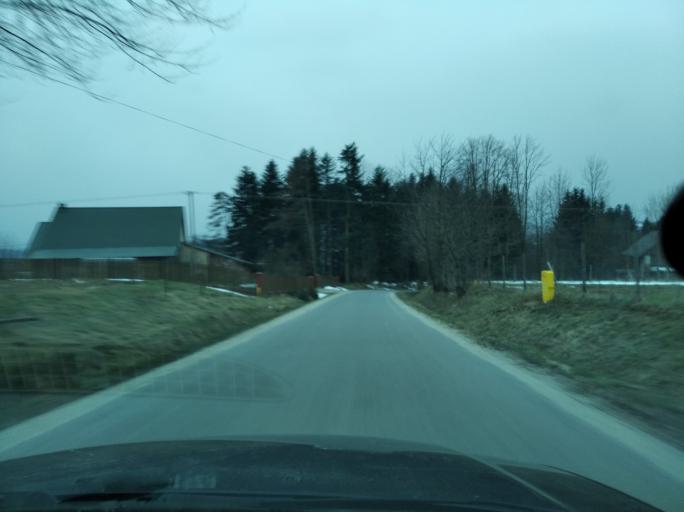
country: PL
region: Subcarpathian Voivodeship
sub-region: Powiat strzyzowski
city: Polomia
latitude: 49.9075
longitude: 21.9004
